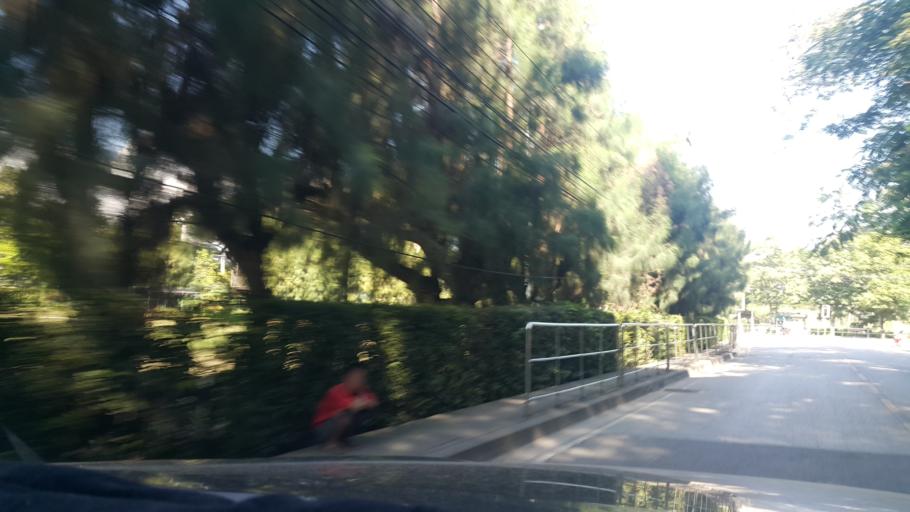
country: TH
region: Chiang Mai
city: Chiang Mai
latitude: 18.7994
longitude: 99.0077
